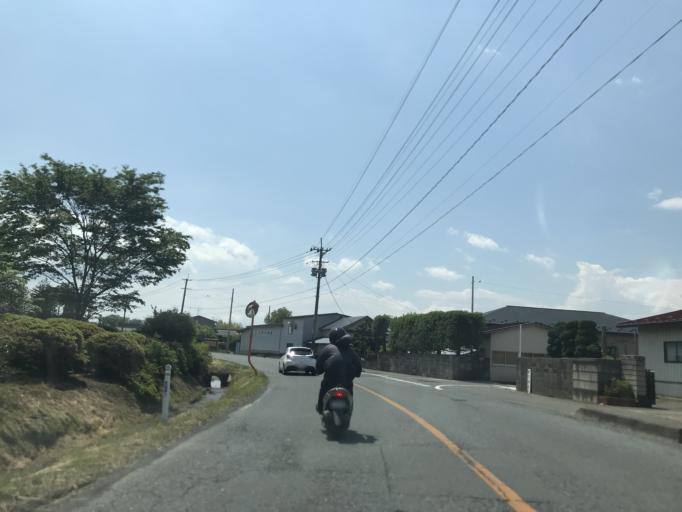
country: JP
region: Miyagi
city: Kogota
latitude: 38.5766
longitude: 141.0333
